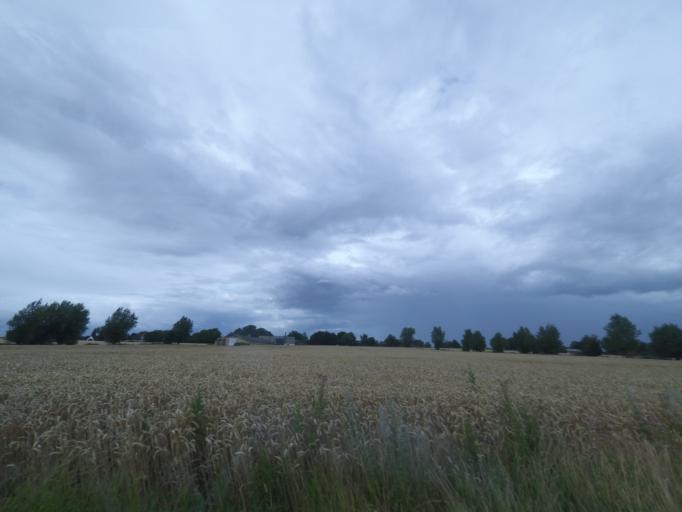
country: DK
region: South Denmark
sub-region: Nordfyns Kommune
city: Otterup
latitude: 55.4865
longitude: 10.3534
